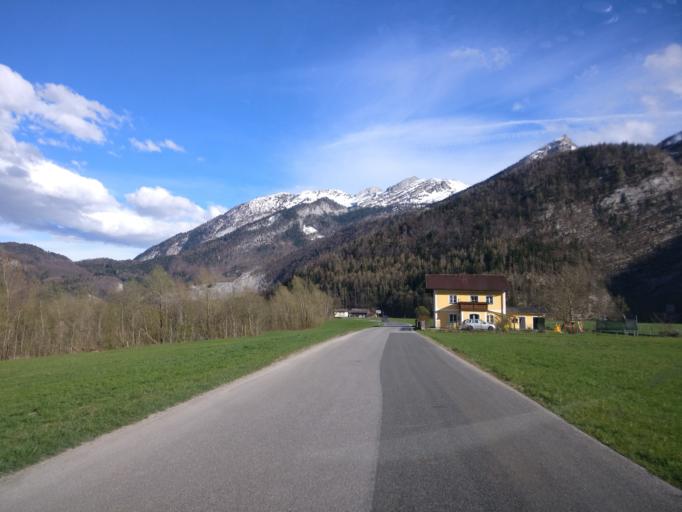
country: AT
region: Salzburg
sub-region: Politischer Bezirk Hallein
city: Golling an der Salzach
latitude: 47.5840
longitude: 13.1601
